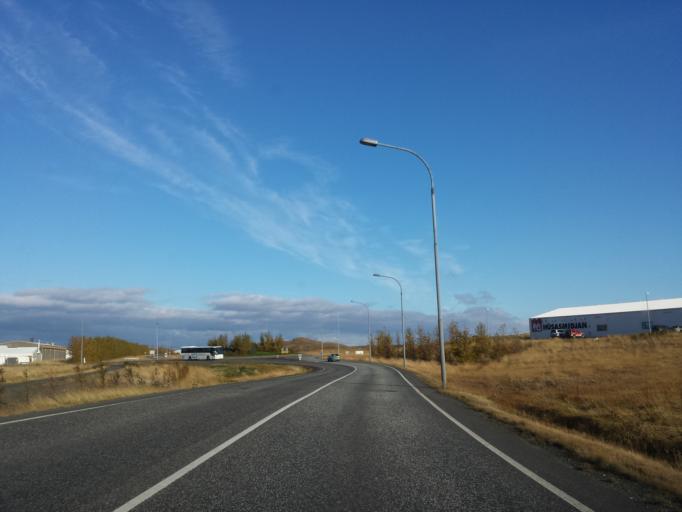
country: IS
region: West
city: Borgarnes
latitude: 64.5588
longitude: -21.8985
